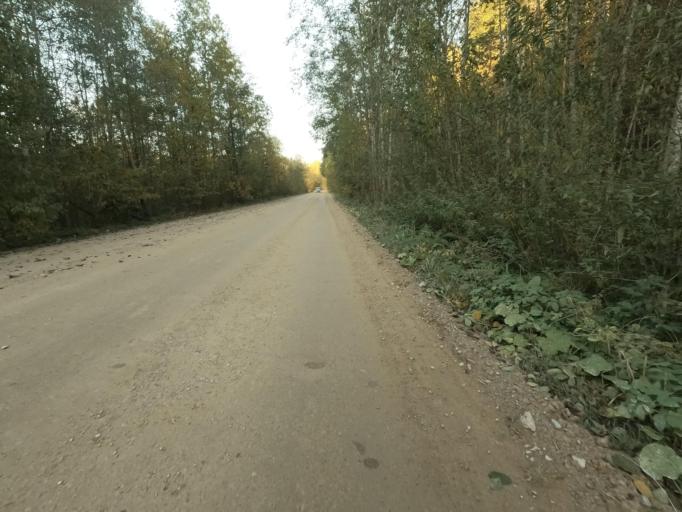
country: RU
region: Leningrad
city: Lyuban'
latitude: 58.9900
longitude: 31.1032
